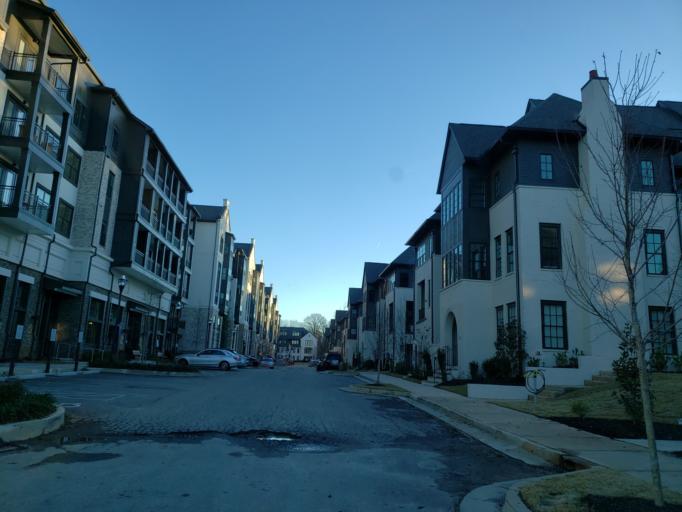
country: US
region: Georgia
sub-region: Fulton County
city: Sandy Springs
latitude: 33.9345
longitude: -84.3654
